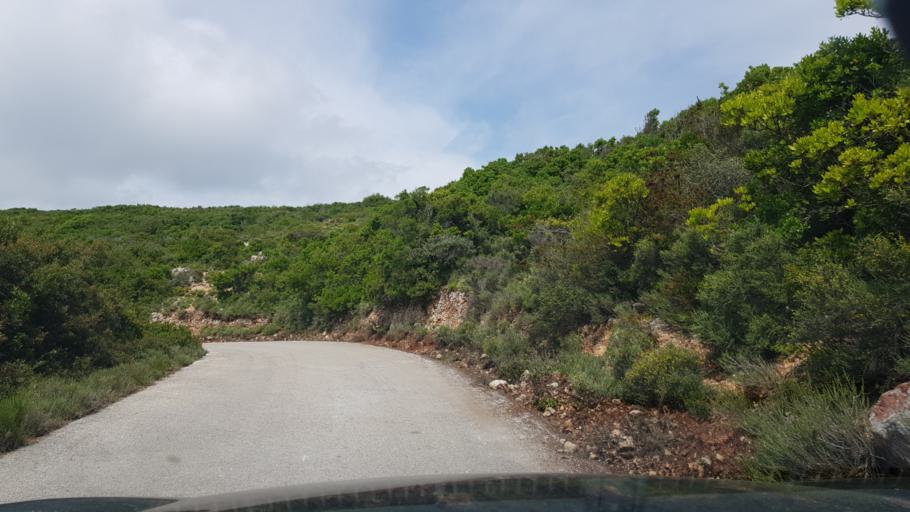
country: GR
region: Ionian Islands
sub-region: Lefkada
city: Nidri
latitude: 38.6010
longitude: 20.5598
